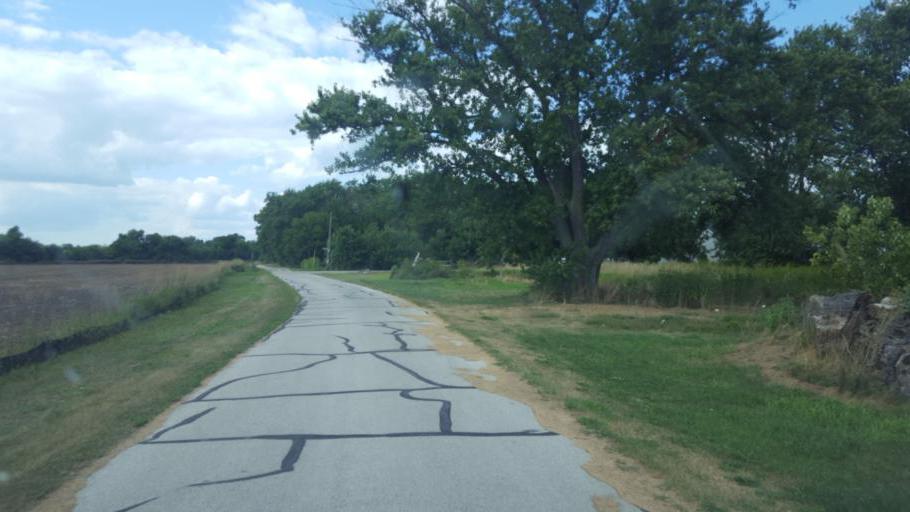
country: US
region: Ohio
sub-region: Lucas County
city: Curtice
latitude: 41.6548
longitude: -83.2498
